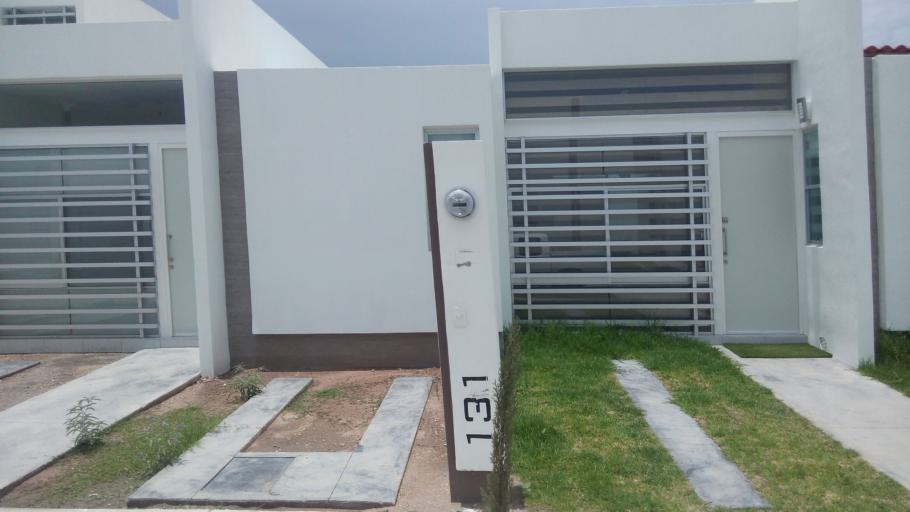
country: MX
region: Aguascalientes
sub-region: Aguascalientes
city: San Sebastian [Fraccionamiento]
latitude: 21.8315
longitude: -102.3169
